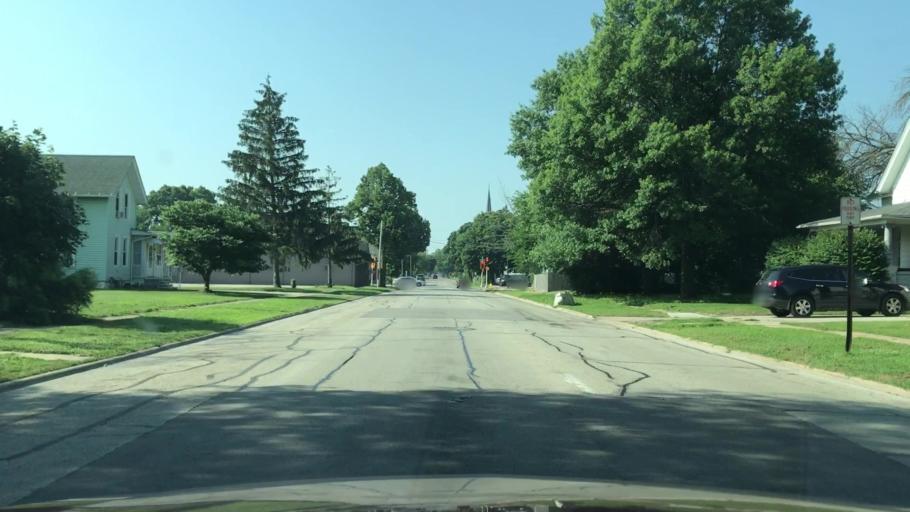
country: US
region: Illinois
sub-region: Winnebago County
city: Rockford
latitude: 42.2535
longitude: -89.0824
